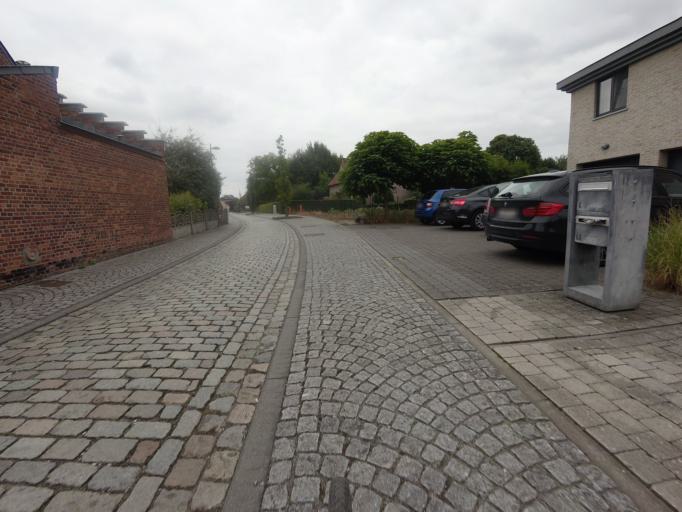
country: BE
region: Flanders
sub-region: Provincie Vlaams-Brabant
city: Bertem
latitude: 50.9035
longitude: 4.6122
